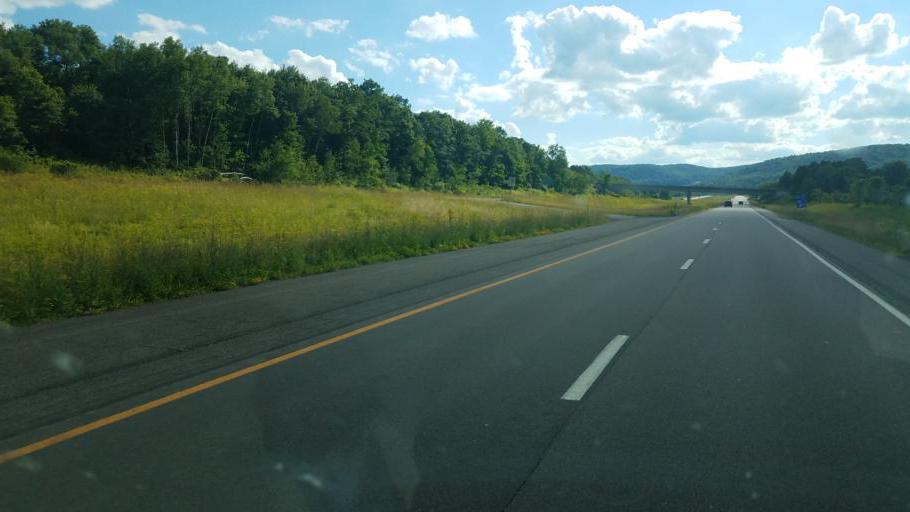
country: US
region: New York
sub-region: Allegany County
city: Cuba
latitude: 42.1792
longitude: -78.3676
